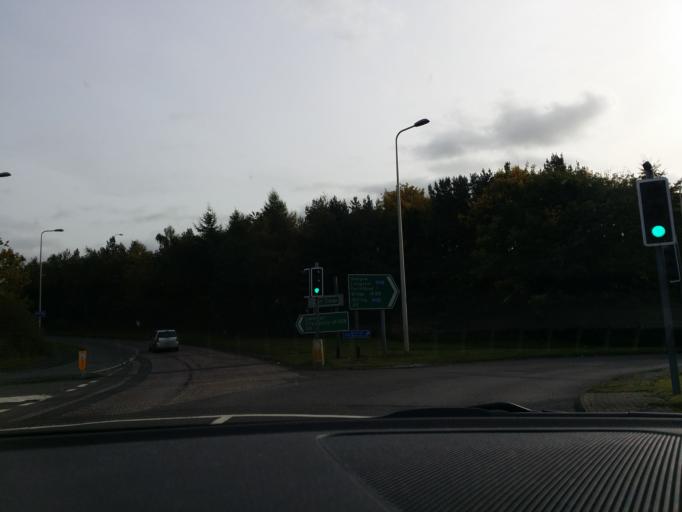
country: GB
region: Scotland
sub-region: Edinburgh
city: Ratho
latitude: 55.9377
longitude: -3.3582
